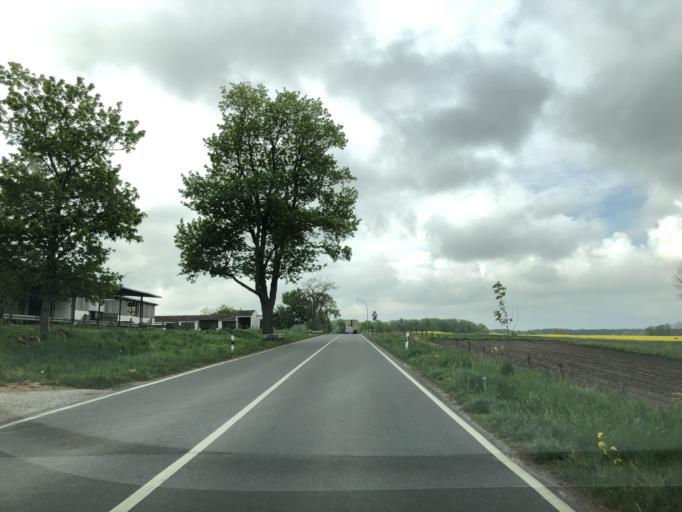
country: DE
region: Mecklenburg-Vorpommern
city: Muhl Rosin
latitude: 53.7115
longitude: 12.1406
